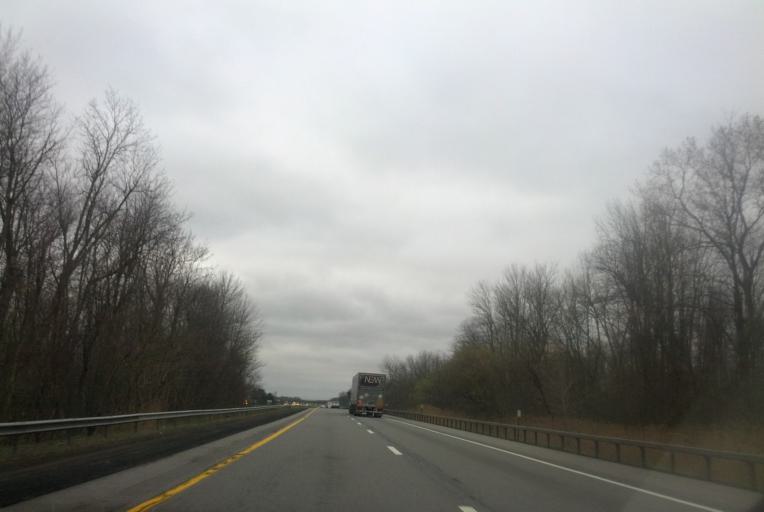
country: US
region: New York
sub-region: Ontario County
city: Manchester
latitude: 42.9780
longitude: -77.2126
